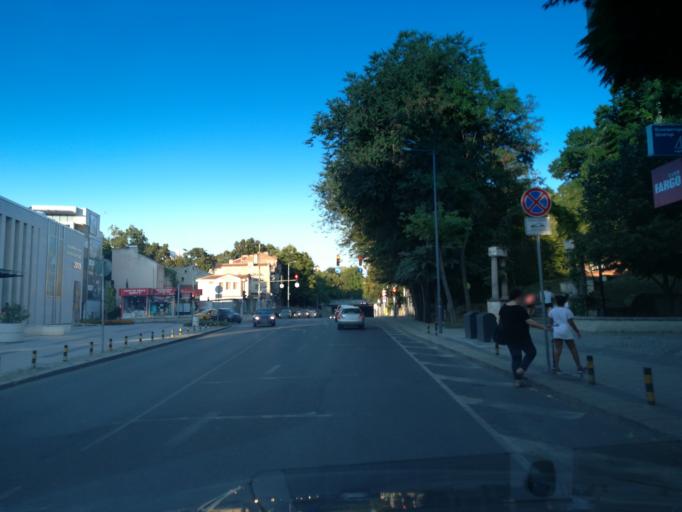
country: BG
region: Plovdiv
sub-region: Obshtina Plovdiv
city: Plovdiv
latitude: 42.1427
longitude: 24.7453
